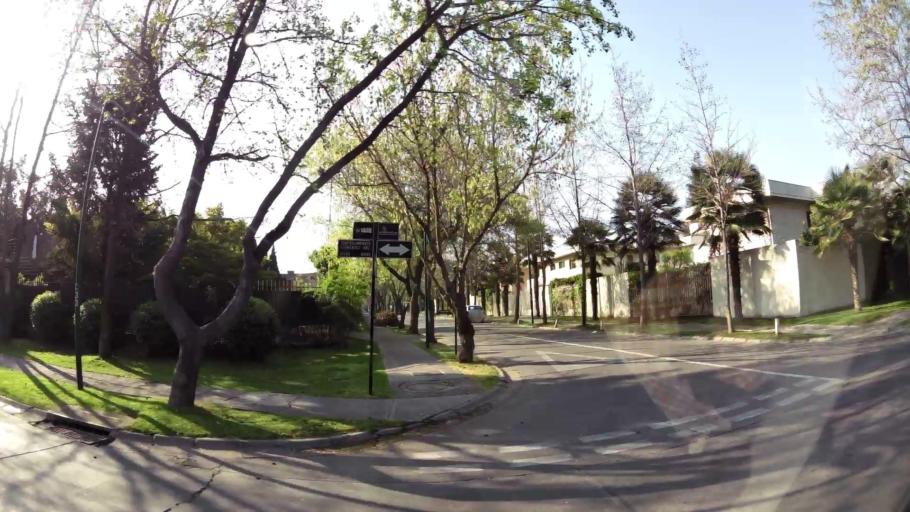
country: CL
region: Santiago Metropolitan
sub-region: Provincia de Santiago
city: Villa Presidente Frei, Nunoa, Santiago, Chile
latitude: -33.3639
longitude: -70.5371
